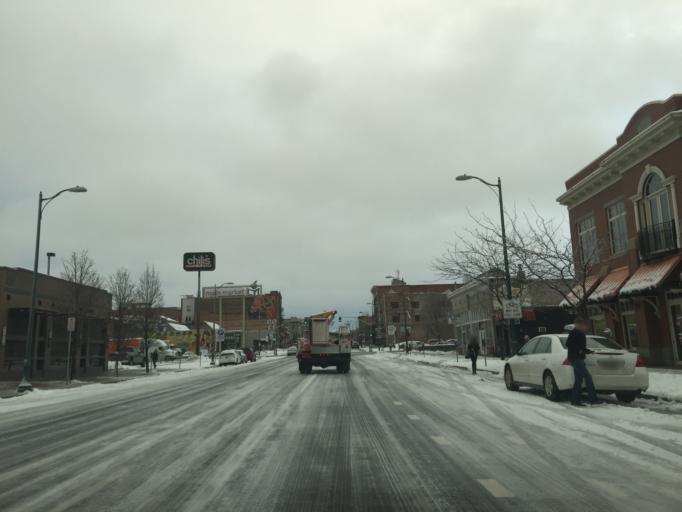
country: US
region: Washington
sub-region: Spokane County
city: Spokane
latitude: 47.6591
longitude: -117.4148
